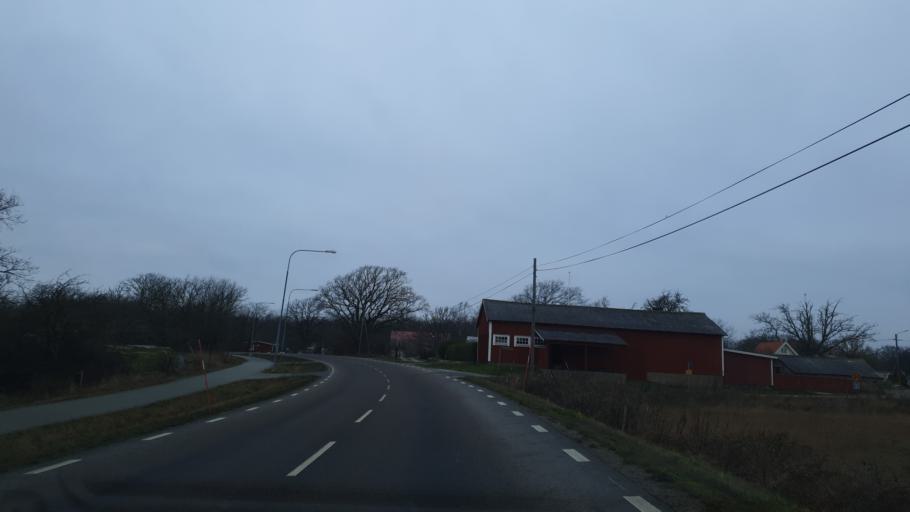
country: SE
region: Blekinge
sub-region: Karlskrona Kommun
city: Sturko
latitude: 56.1150
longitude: 15.6714
